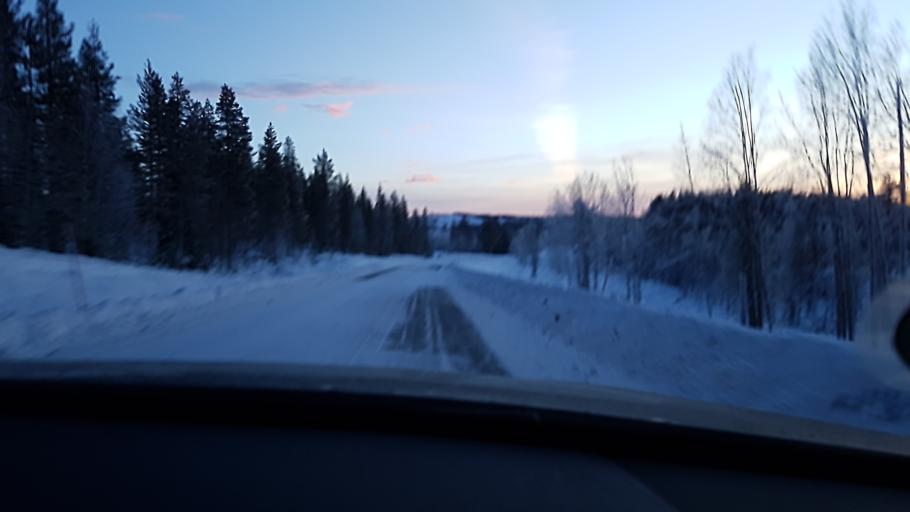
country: SE
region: Vaesterbotten
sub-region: Storumans Kommun
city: Storuman
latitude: 65.1486
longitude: 17.2604
